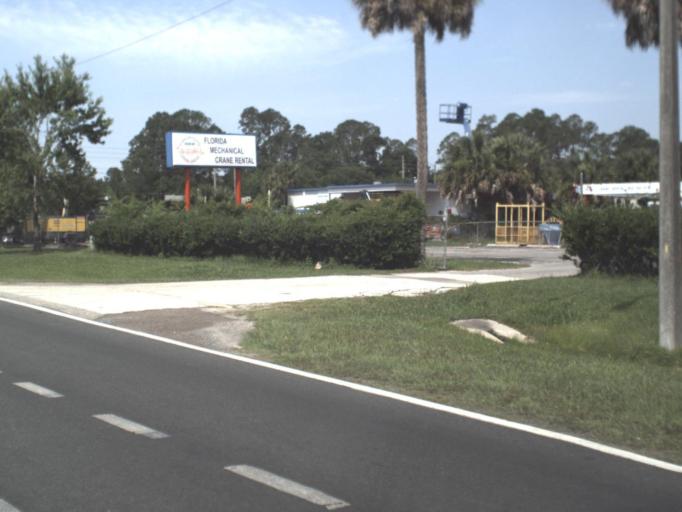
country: US
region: Florida
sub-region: Alachua County
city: Gainesville
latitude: 29.6861
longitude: -82.2886
